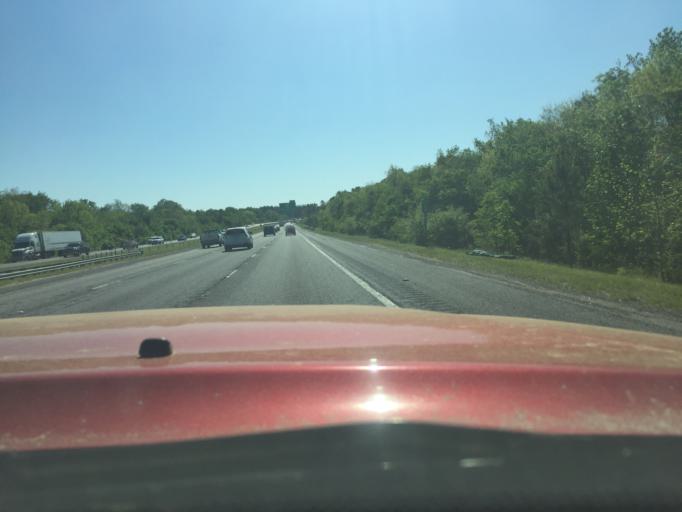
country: US
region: South Carolina
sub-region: Lexington County
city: Cayce
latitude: 33.9315
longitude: -81.0199
